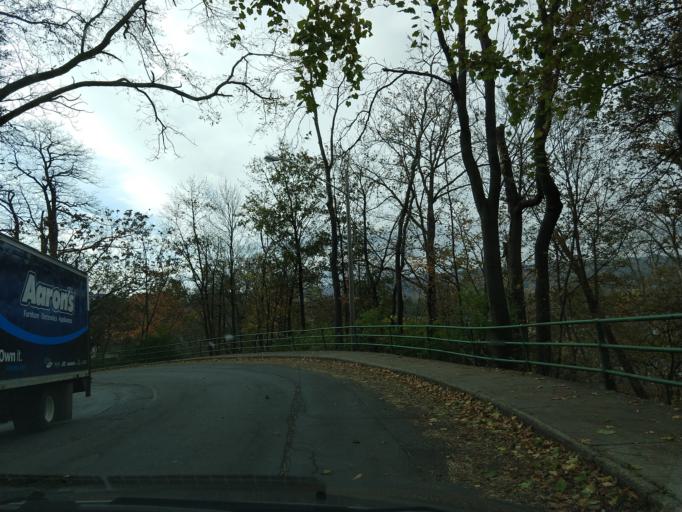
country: US
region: New York
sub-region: Tompkins County
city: Ithaca
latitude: 42.4446
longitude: -76.4939
